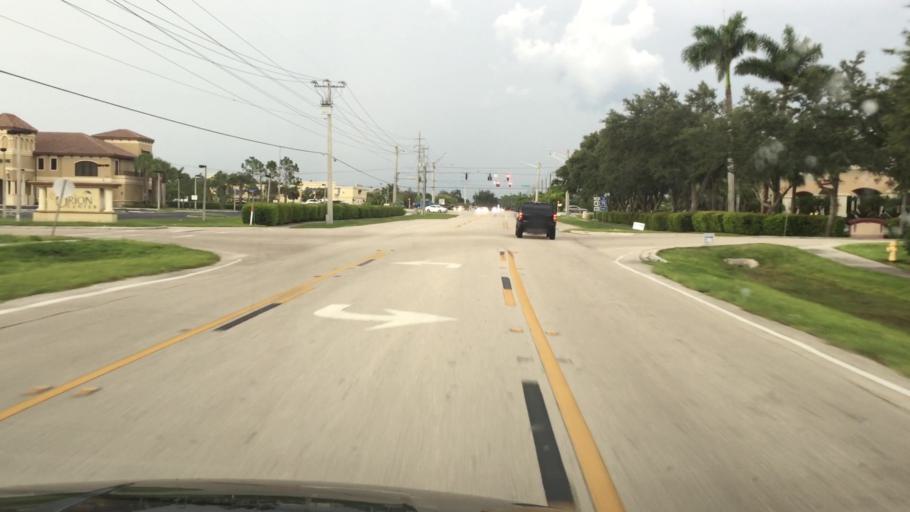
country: US
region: Florida
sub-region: Lee County
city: Villas
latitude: 26.5448
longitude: -81.8468
